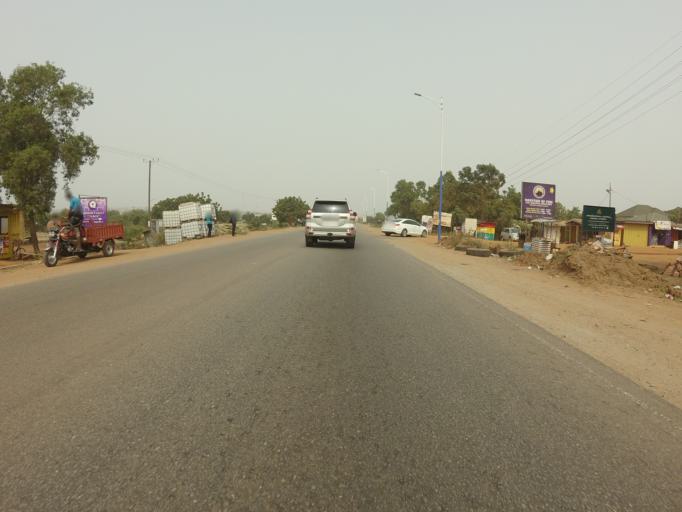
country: GH
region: Greater Accra
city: Tema
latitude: 5.7585
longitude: 0.0500
